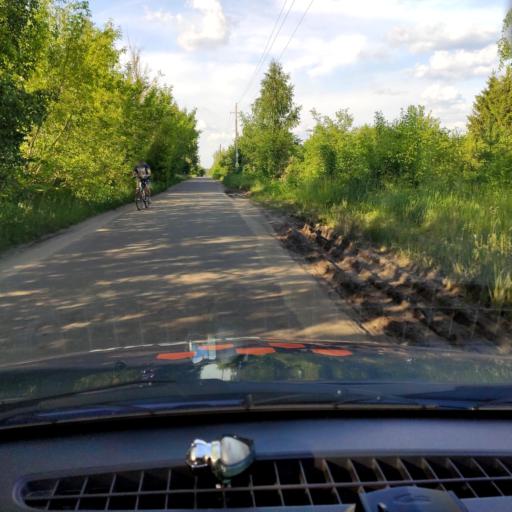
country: RU
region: Voronezj
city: Ramon'
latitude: 51.8508
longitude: 39.2385
